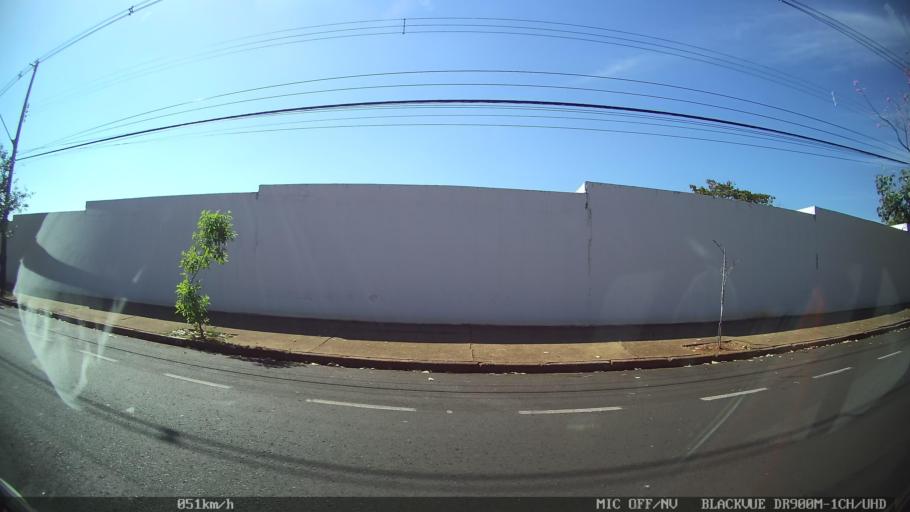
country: BR
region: Sao Paulo
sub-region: Sao Jose Do Rio Preto
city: Sao Jose do Rio Preto
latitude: -20.8141
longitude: -49.4106
